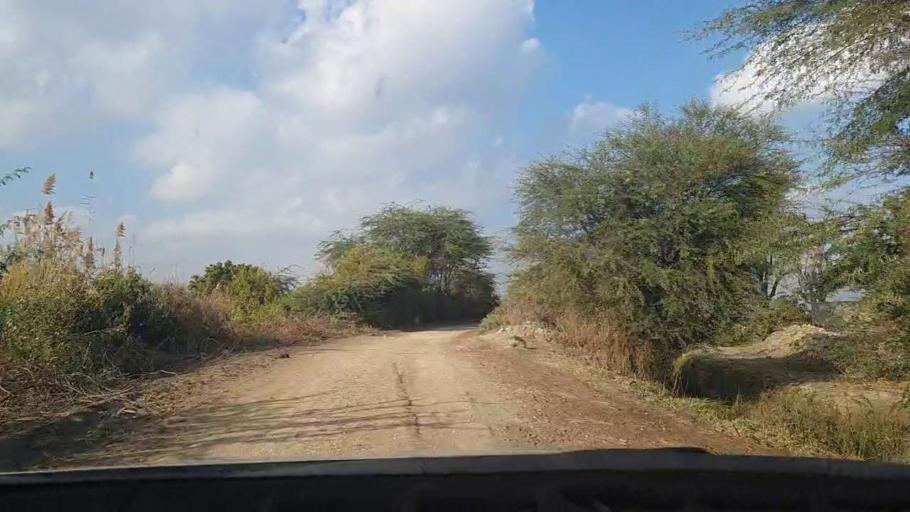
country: PK
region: Sindh
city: Tando Mittha Khan
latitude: 25.9066
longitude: 69.3076
